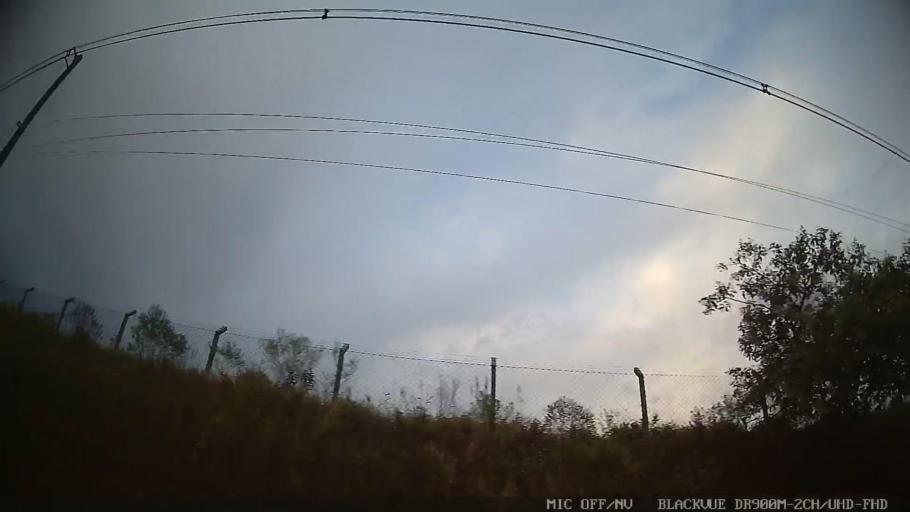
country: BR
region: Sao Paulo
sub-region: Vinhedo
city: Vinhedo
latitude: -23.0203
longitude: -46.9133
